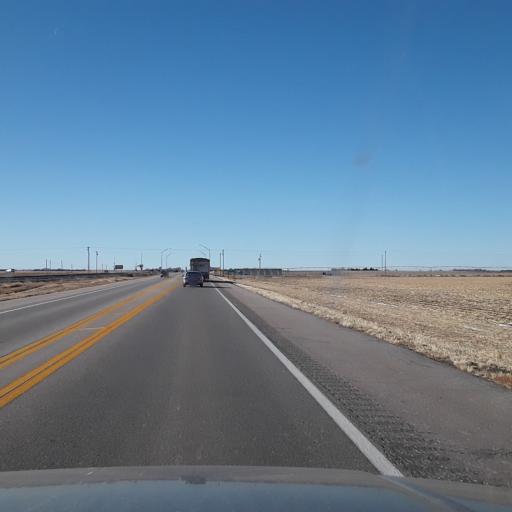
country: US
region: Nebraska
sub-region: Kearney County
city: Minden
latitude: 40.4740
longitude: -99.1565
